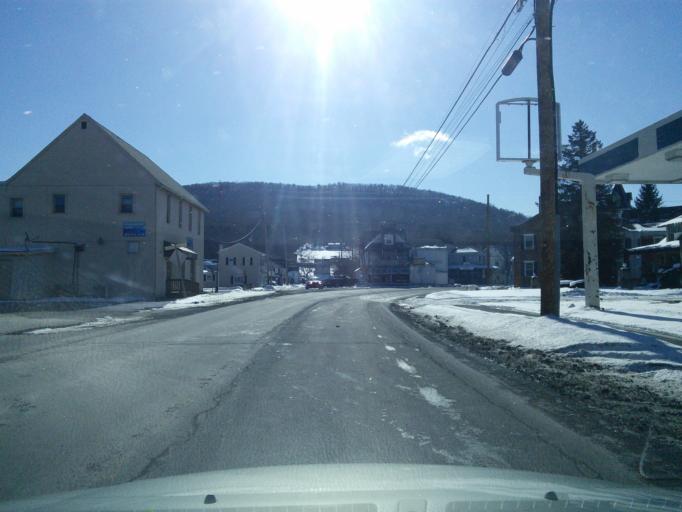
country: US
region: Pennsylvania
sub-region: Centre County
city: Milesburg
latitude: 40.9421
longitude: -77.7857
